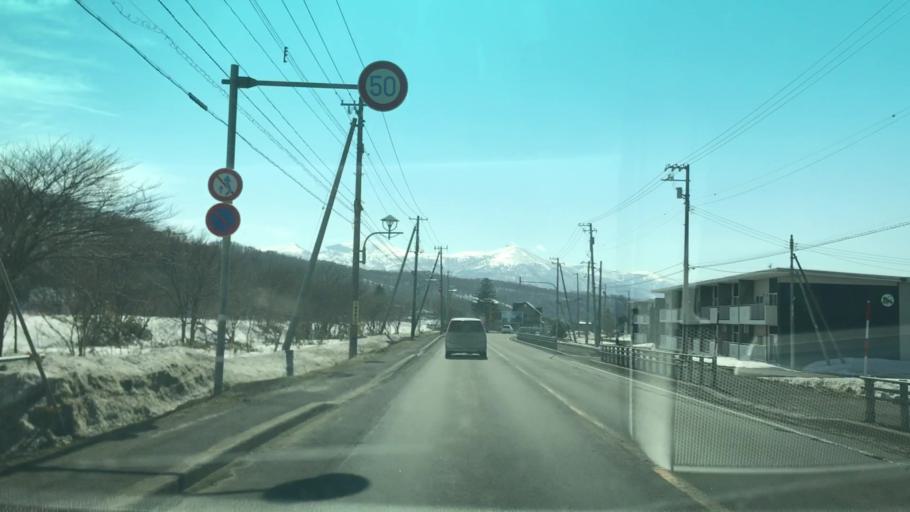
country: JP
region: Hokkaido
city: Iwanai
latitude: 42.9802
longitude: 140.6466
